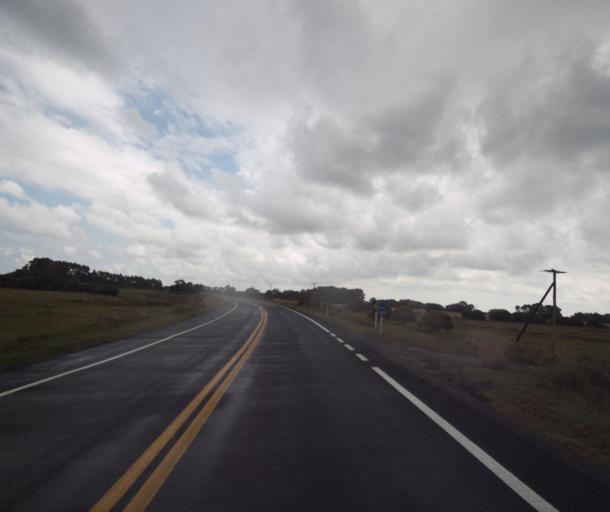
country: BR
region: Rio Grande do Sul
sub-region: Tapes
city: Tapes
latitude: -31.3156
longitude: -51.1190
